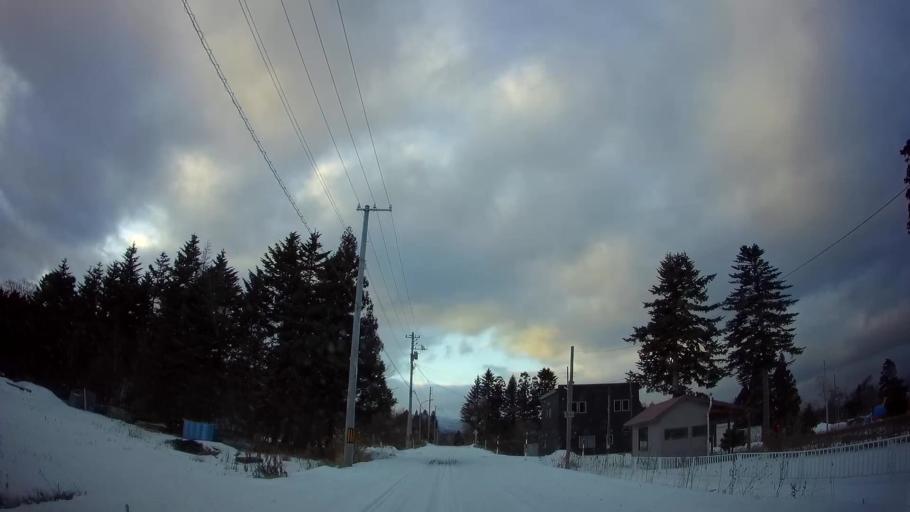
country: JP
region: Hokkaido
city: Nanae
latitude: 42.0213
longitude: 140.8369
